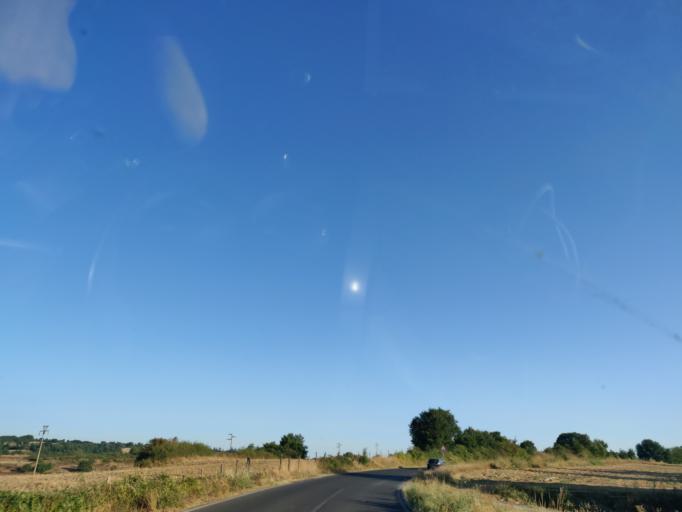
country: IT
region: Latium
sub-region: Provincia di Viterbo
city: Grotte di Castro
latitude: 42.7023
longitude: 11.8805
